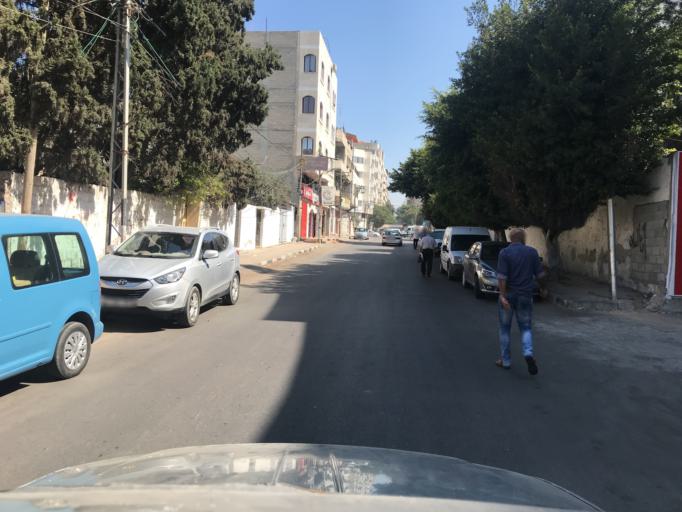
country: PS
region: Gaza Strip
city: Gaza
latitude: 31.5203
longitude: 34.4485
